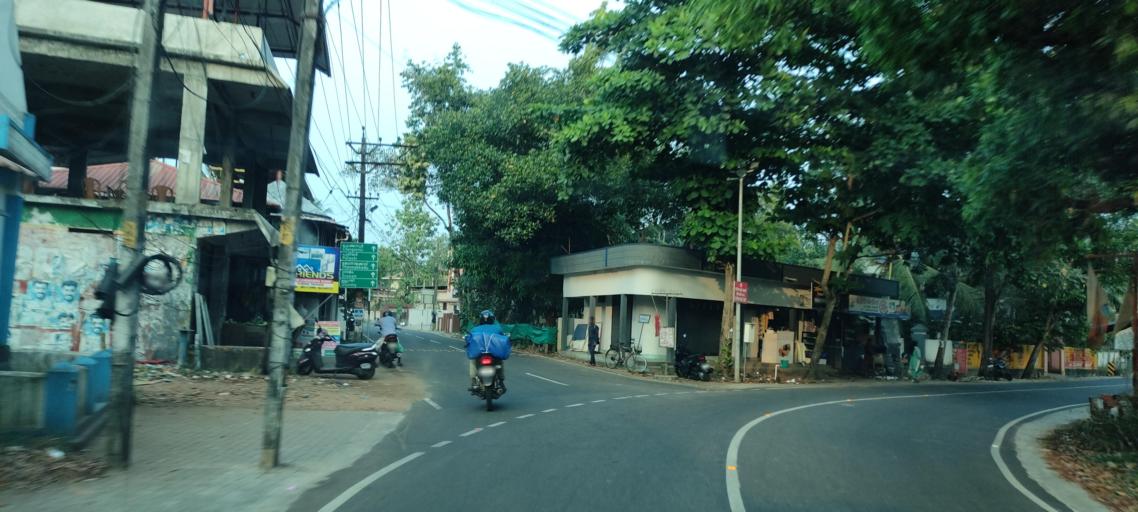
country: IN
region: Kerala
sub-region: Alappuzha
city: Mavelikara
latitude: 9.2626
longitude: 76.5558
